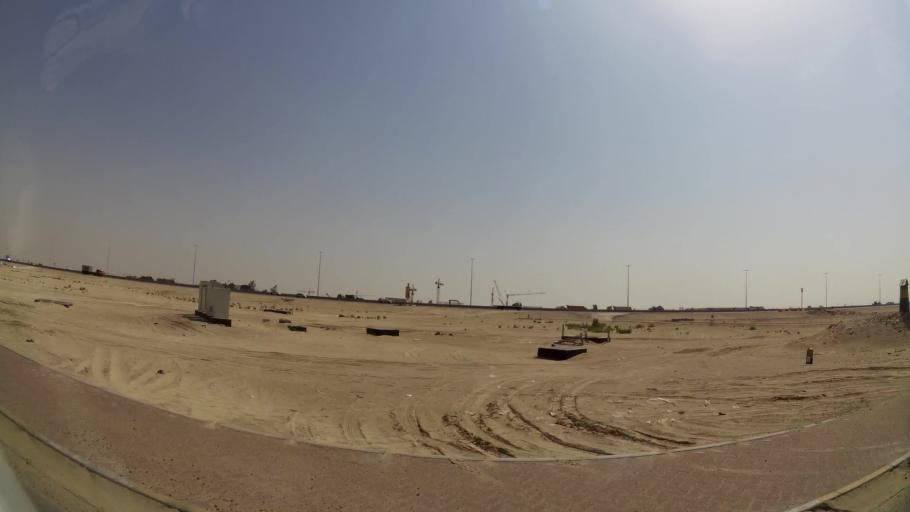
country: AE
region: Abu Dhabi
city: Abu Dhabi
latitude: 24.2954
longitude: 54.5693
